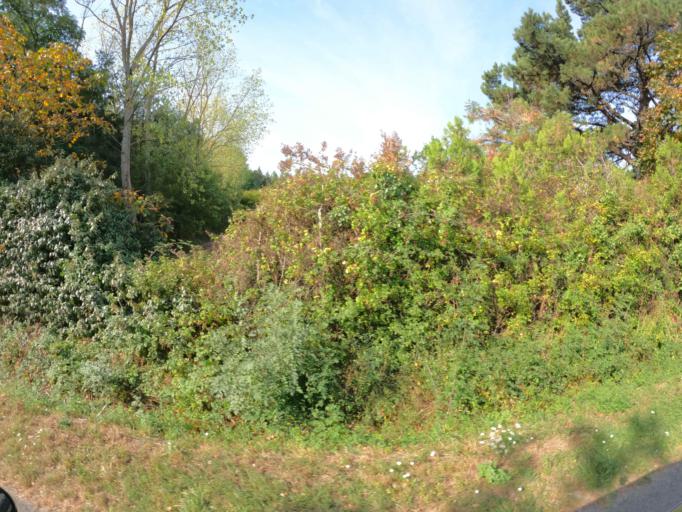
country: FR
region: Pays de la Loire
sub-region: Departement de la Vendee
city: Saint-Christophe-du-Ligneron
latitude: 46.8020
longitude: -1.7955
